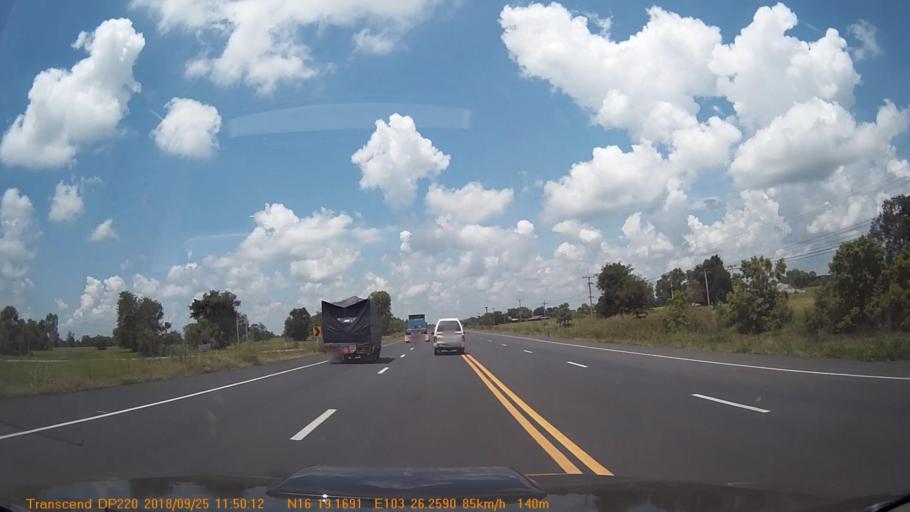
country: TH
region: Kalasin
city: Khong Chai
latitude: 16.3195
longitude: 103.4376
